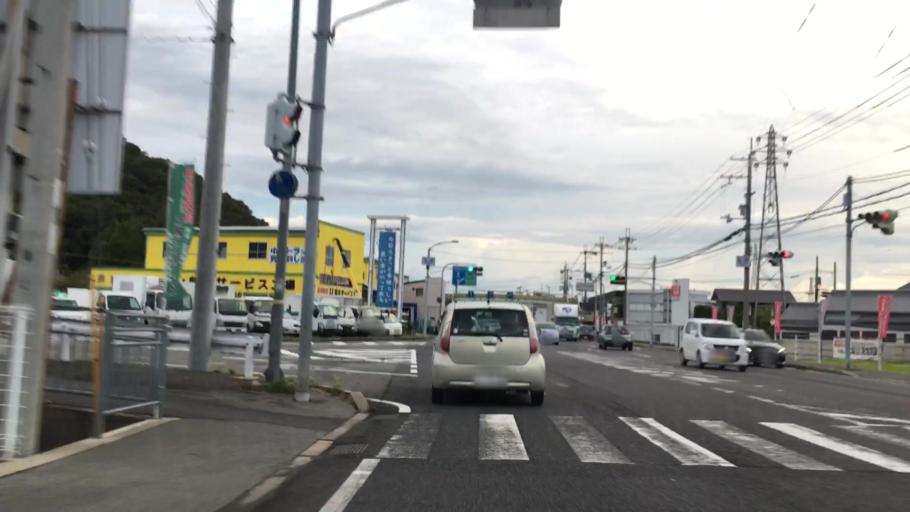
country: JP
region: Hyogo
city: Himeji
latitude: 34.8706
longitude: 134.7292
